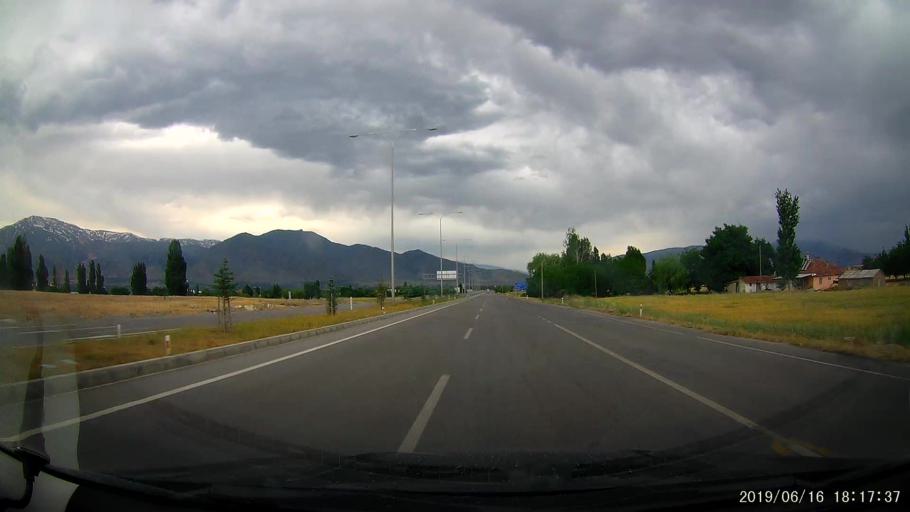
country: TR
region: Erzincan
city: Erzincan
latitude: 39.7310
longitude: 39.5299
